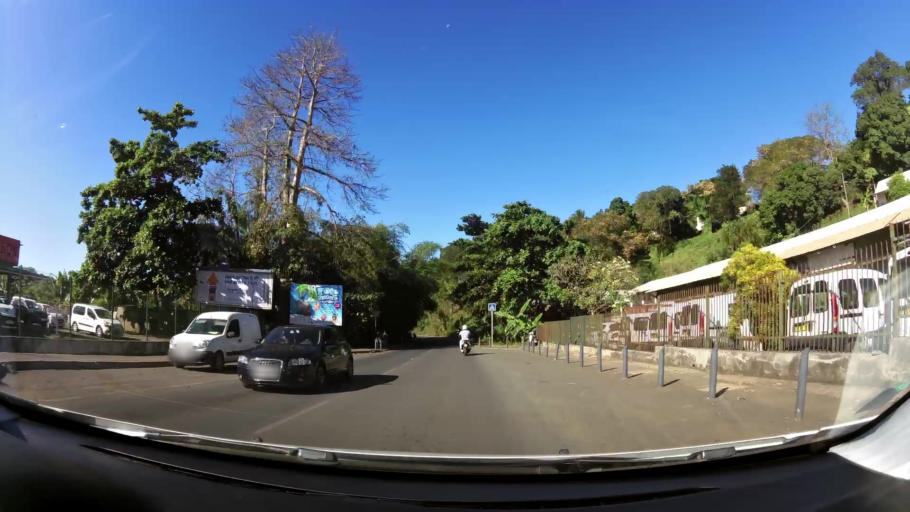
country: YT
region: Mamoudzou
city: Mamoudzou
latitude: -12.7758
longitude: 45.2271
